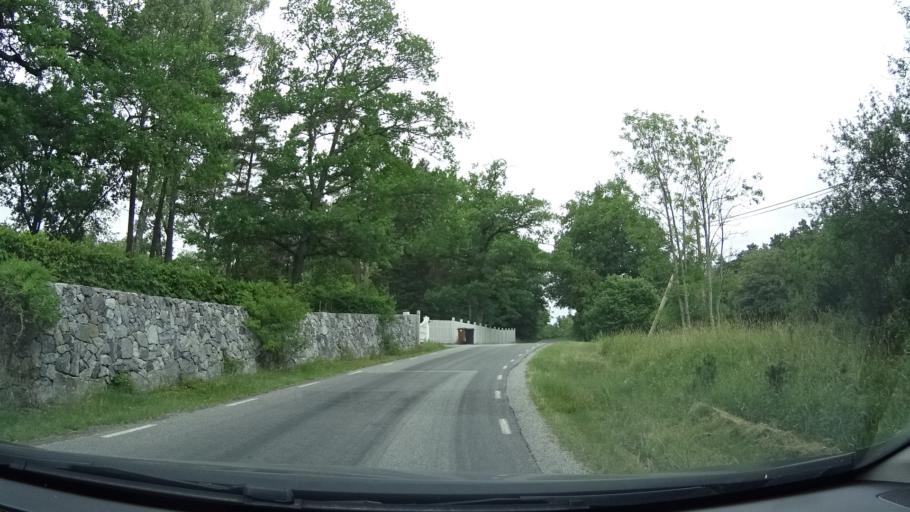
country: SE
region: Stockholm
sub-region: Varmdo Kommun
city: Mortnas
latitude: 59.3755
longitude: 18.4644
